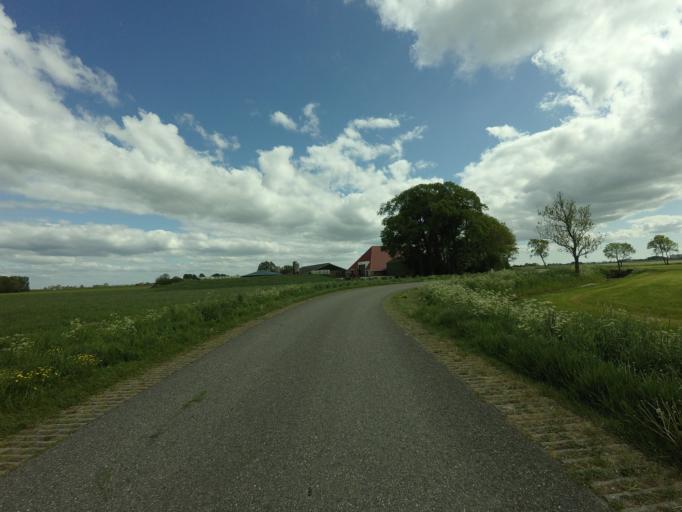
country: NL
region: Friesland
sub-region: Sudwest Fryslan
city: Bolsward
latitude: 53.0797
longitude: 5.5512
